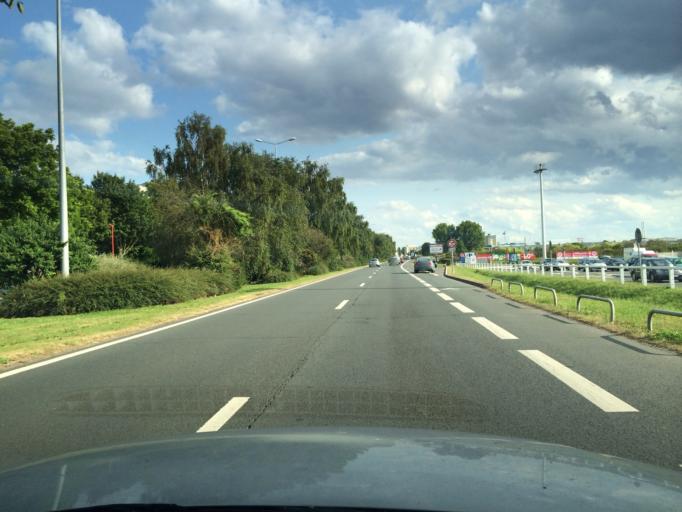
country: FR
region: Lower Normandy
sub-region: Departement du Calvados
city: Epron
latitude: 49.2096
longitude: -0.3630
